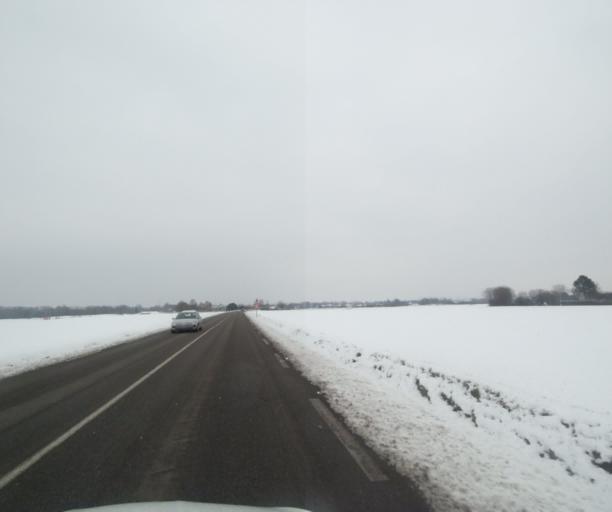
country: FR
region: Champagne-Ardenne
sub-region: Departement de la Haute-Marne
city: Saint-Dizier
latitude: 48.6231
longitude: 4.9295
